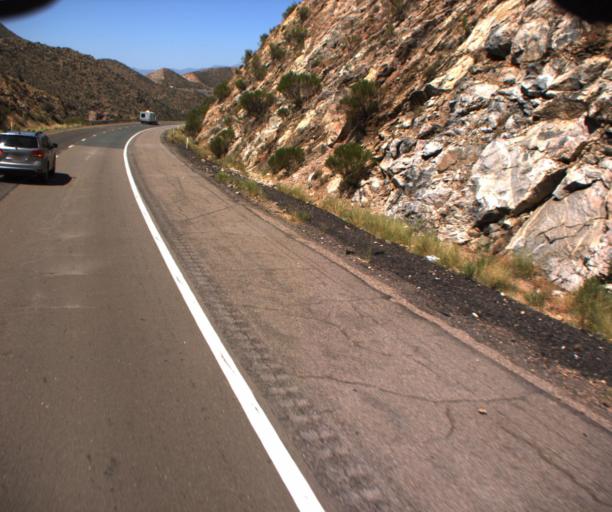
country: US
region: Arizona
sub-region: Mohave County
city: Peach Springs
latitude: 35.1721
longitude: -113.5096
